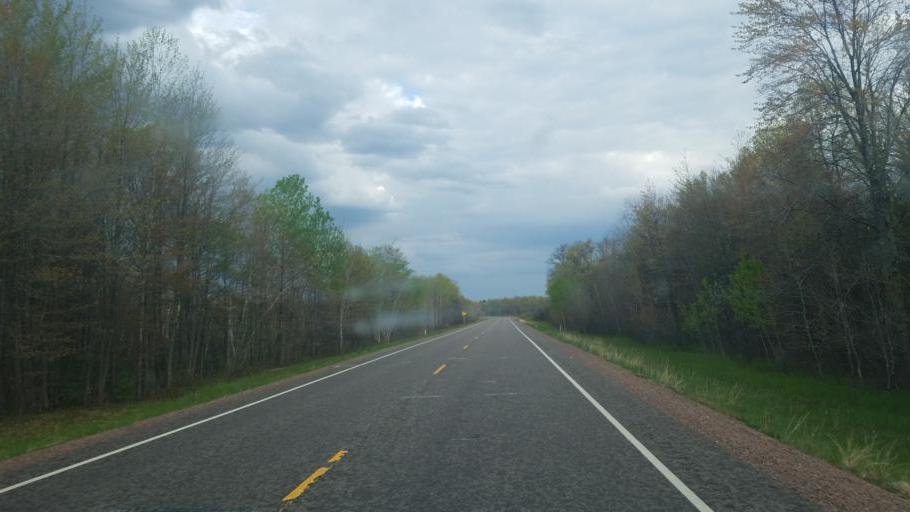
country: US
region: Wisconsin
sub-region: Wood County
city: Nekoosa
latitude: 44.3797
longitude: -90.1341
